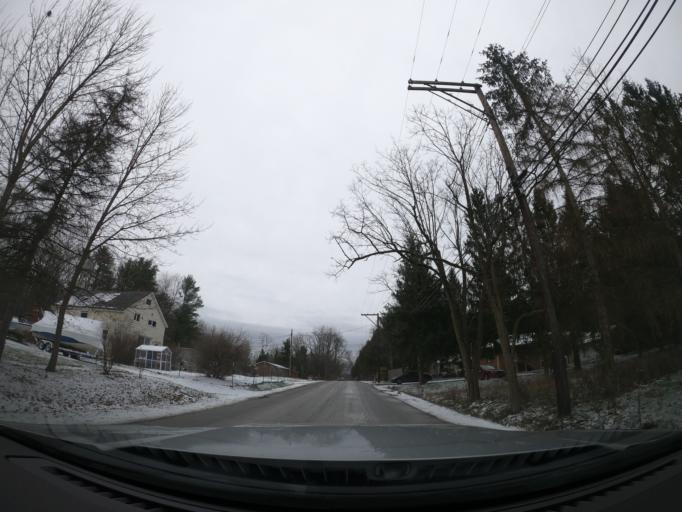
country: US
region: New York
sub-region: Tompkins County
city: Northeast Ithaca
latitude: 42.4701
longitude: -76.4502
